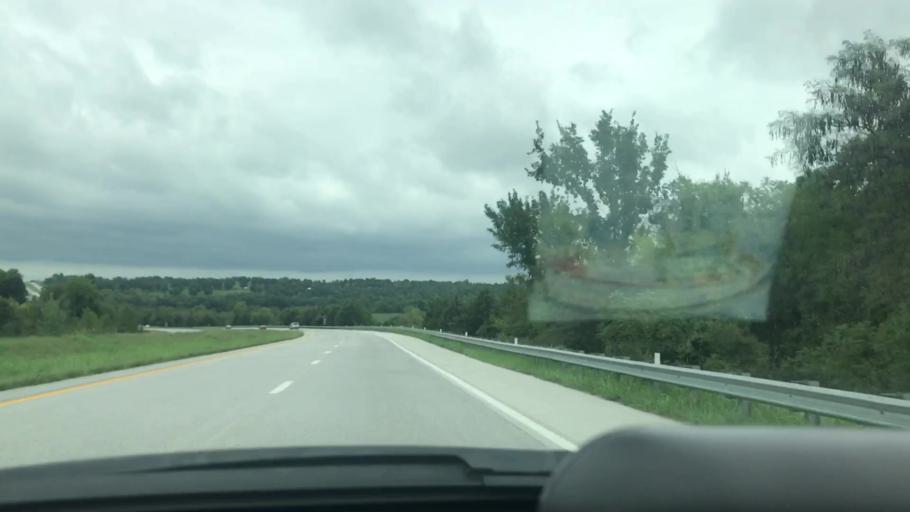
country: US
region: Missouri
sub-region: Greene County
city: Fair Grove
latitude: 37.4063
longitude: -93.1465
